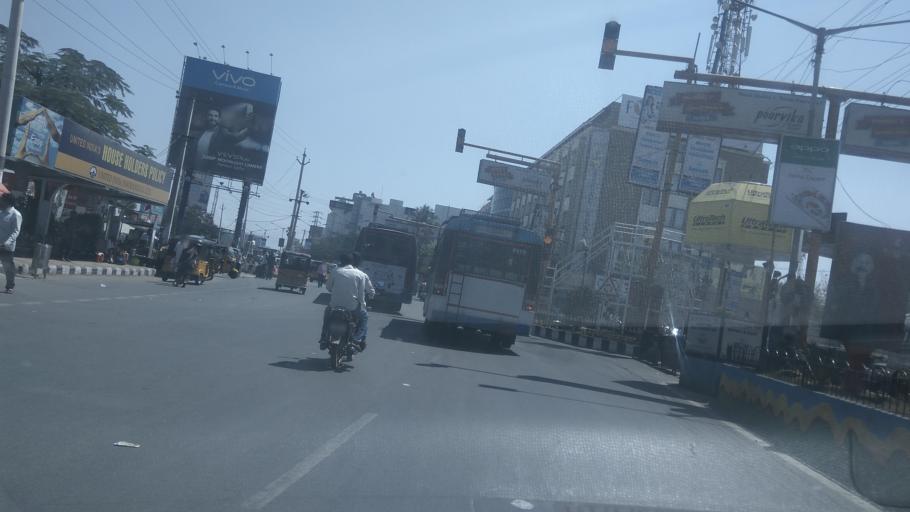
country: IN
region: Andhra Pradesh
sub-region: Chittoor
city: Tirupati
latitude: 13.6287
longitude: 79.4259
